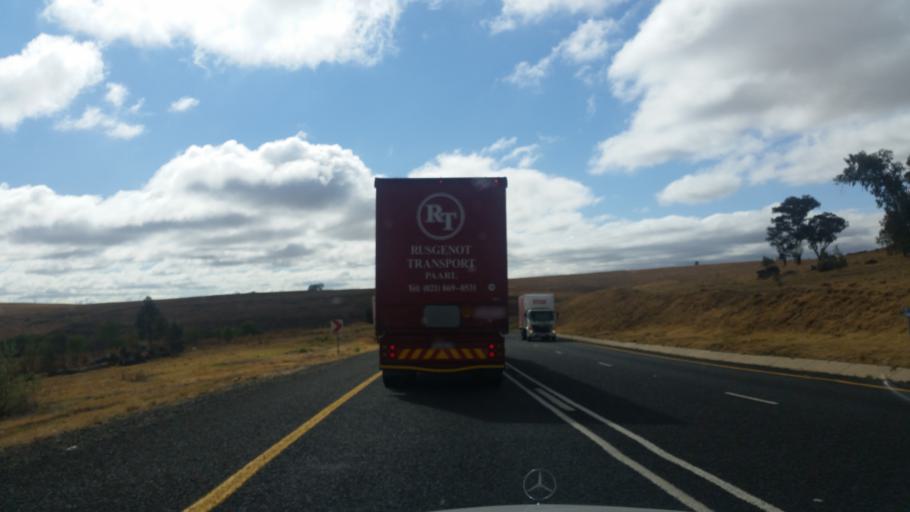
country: ZA
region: Orange Free State
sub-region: Thabo Mofutsanyana District Municipality
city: Phuthaditjhaba
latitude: -28.2715
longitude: 28.8552
